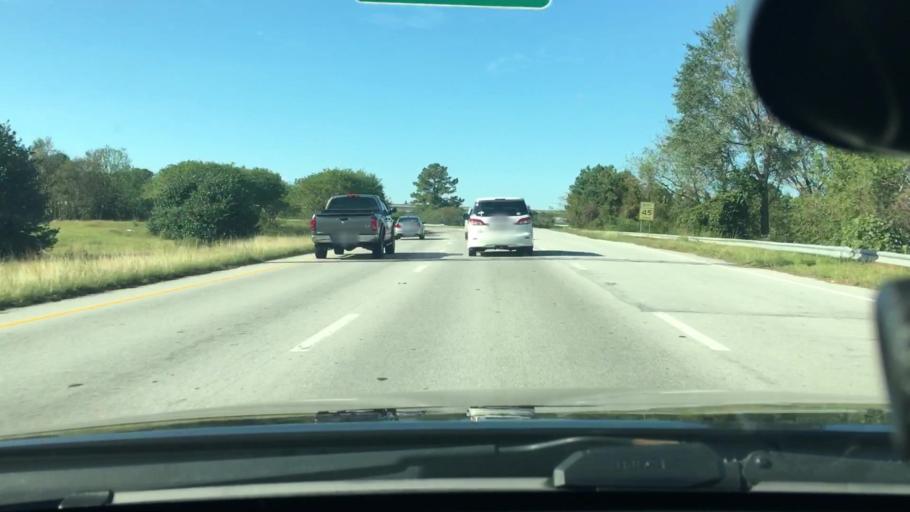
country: US
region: North Carolina
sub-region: Craven County
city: James City
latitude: 35.0913
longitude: -77.0366
